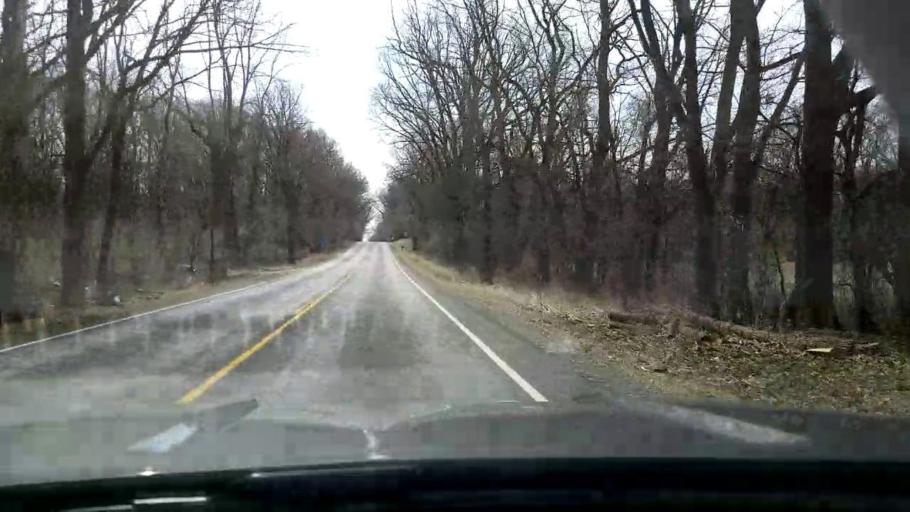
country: US
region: Michigan
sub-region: Jackson County
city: Spring Arbor
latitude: 42.1775
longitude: -84.5203
